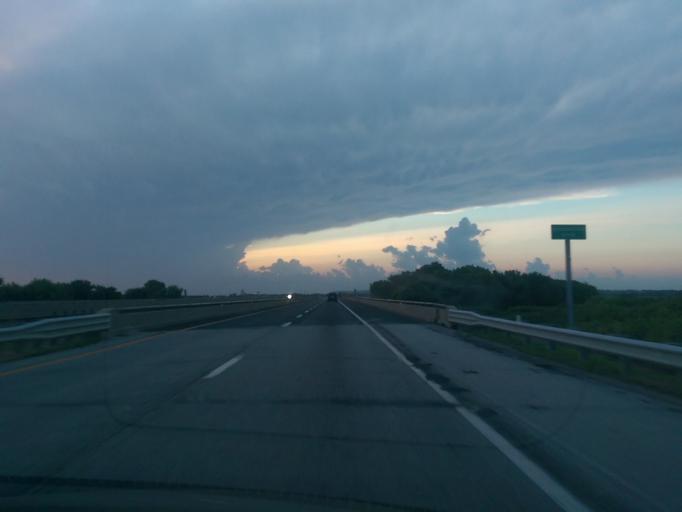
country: US
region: Iowa
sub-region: Fremont County
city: Hamburg
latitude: 40.5688
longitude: -95.6410
